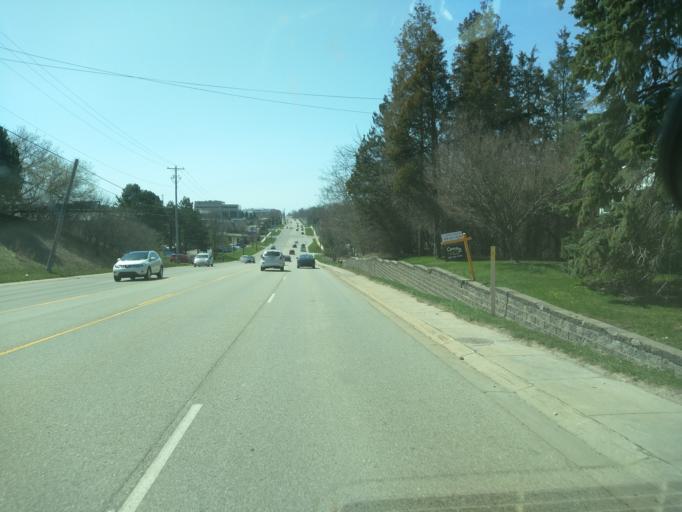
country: US
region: Michigan
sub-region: Kent County
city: East Grand Rapids
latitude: 42.9465
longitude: -85.5707
